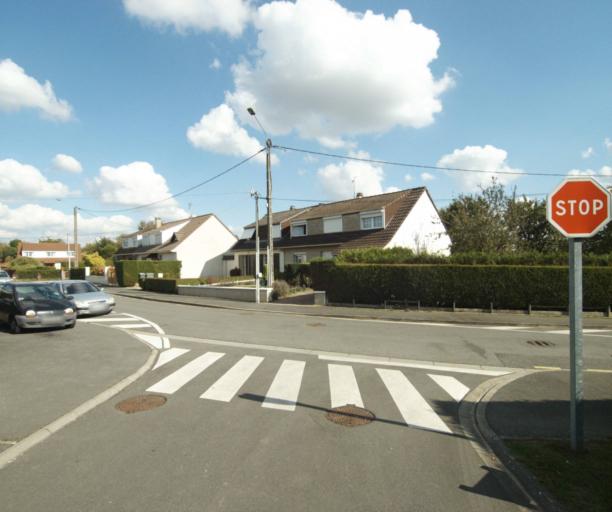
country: FR
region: Nord-Pas-de-Calais
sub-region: Departement du Nord
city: Sainghin-en-Weppes
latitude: 50.5686
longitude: 2.8940
